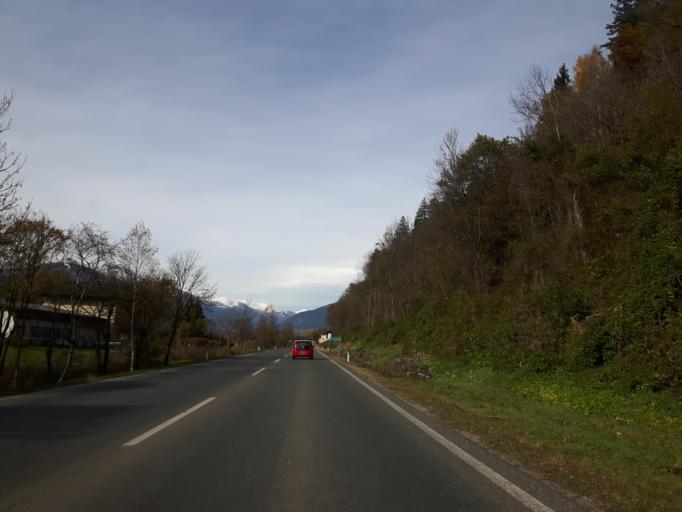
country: AT
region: Tyrol
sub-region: Politischer Bezirk Lienz
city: Lavant
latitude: 46.8059
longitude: 12.8618
